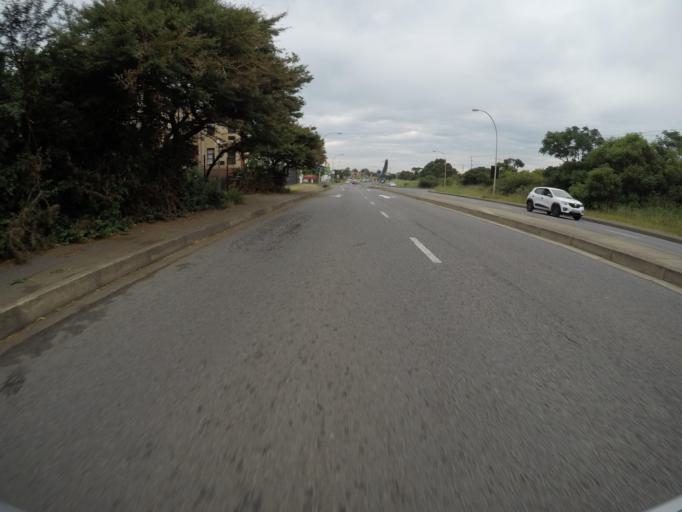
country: ZA
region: Eastern Cape
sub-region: Buffalo City Metropolitan Municipality
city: East London
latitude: -32.9819
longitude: 27.8987
